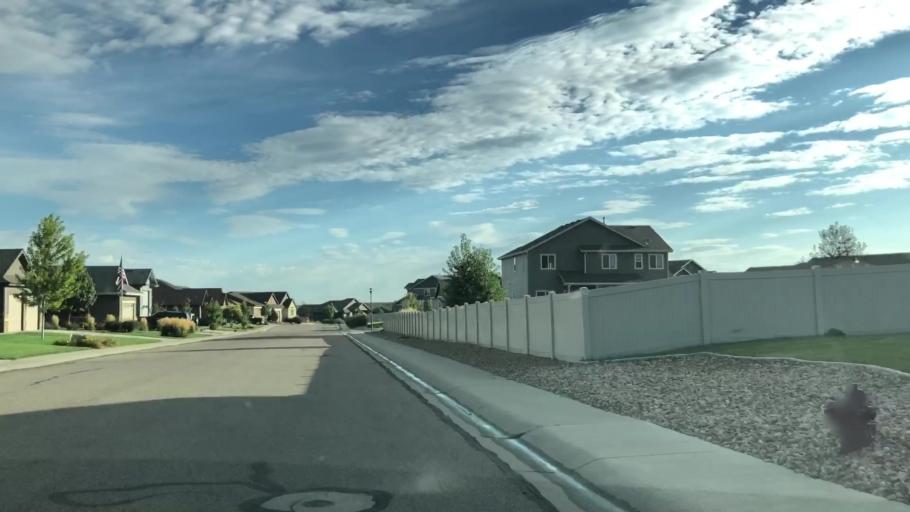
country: US
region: Colorado
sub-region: Weld County
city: Windsor
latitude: 40.4446
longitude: -104.9675
